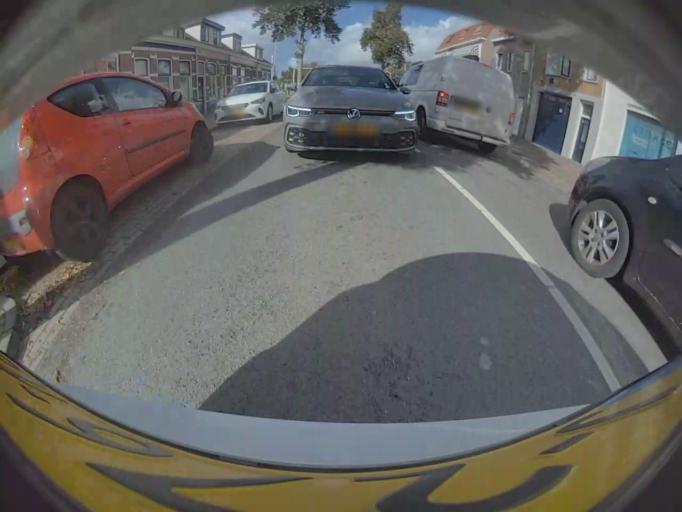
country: NL
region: North Brabant
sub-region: Gemeente Bergen op Zoom
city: Bergen op Zoom
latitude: 51.4929
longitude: 4.2821
